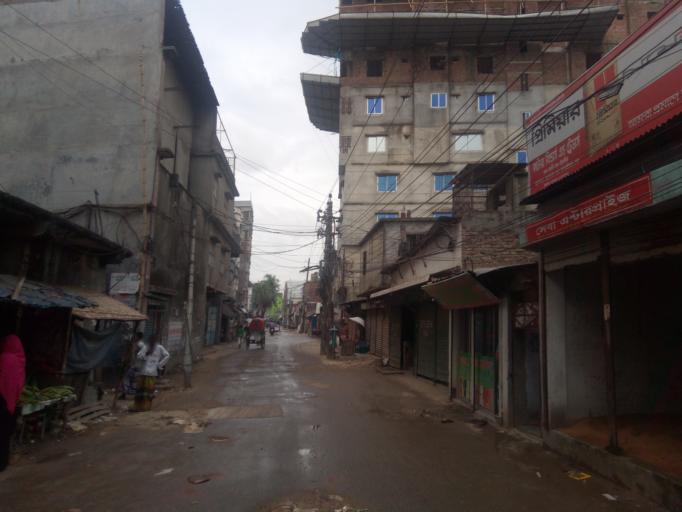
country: BD
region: Dhaka
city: Azimpur
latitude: 23.7092
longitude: 90.3711
